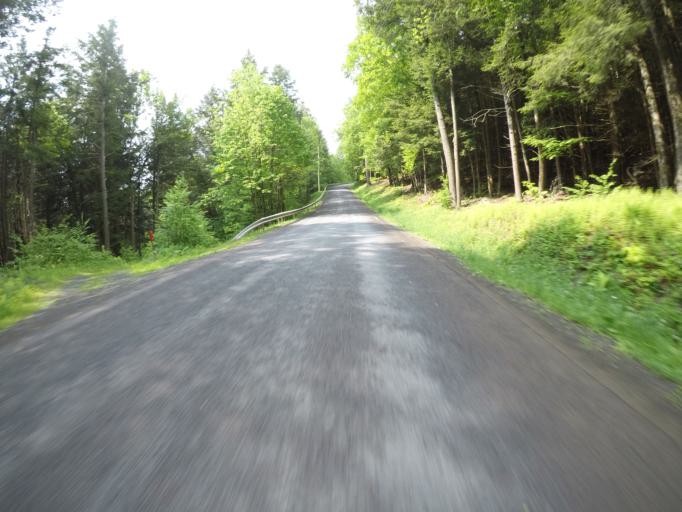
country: US
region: New York
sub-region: Delaware County
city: Stamford
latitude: 42.1541
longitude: -74.6640
